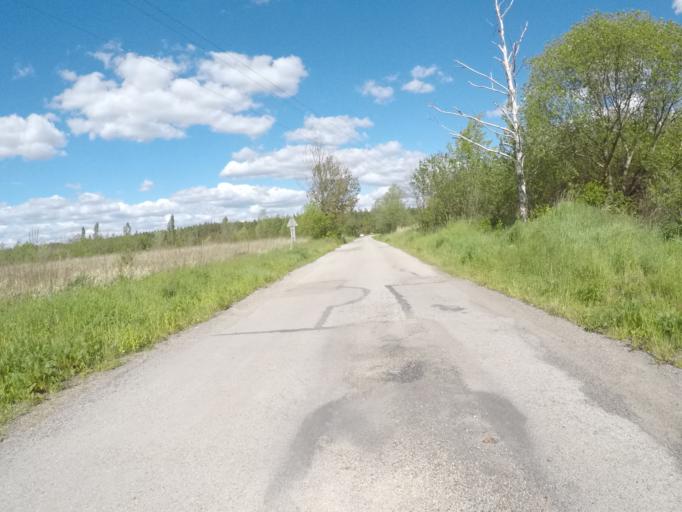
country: PL
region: Swietokrzyskie
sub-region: Powiat kielecki
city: Miedziana Gora
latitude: 50.8842
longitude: 20.5247
